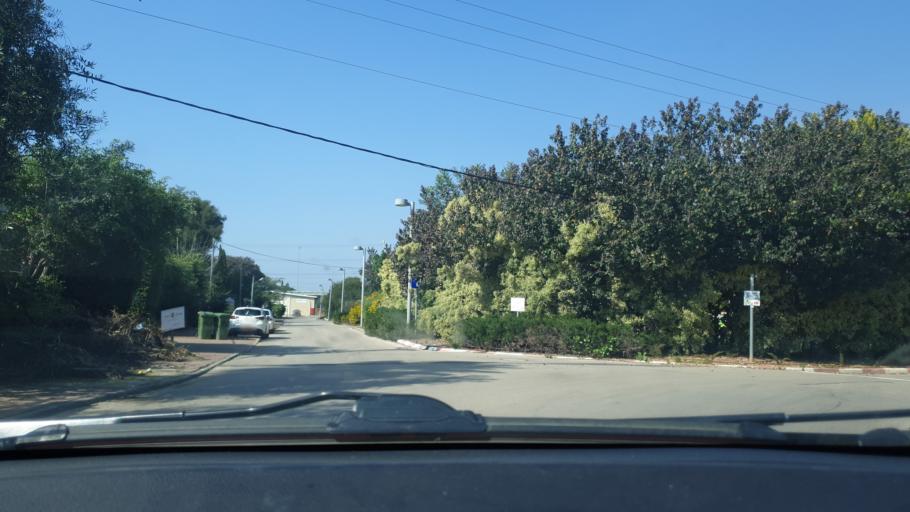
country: IL
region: Central District
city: Bet Dagan
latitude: 32.0094
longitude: 34.8187
